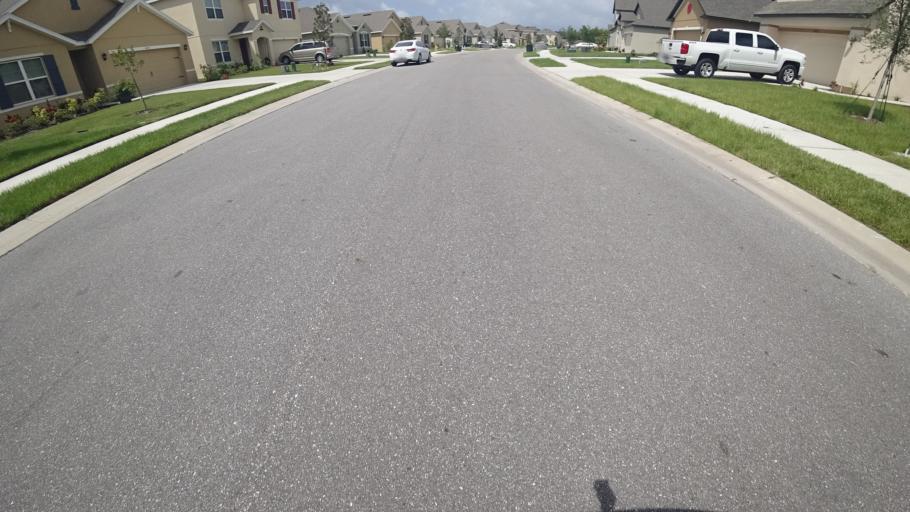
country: US
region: Florida
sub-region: Manatee County
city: Ellenton
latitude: 27.5512
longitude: -82.5184
